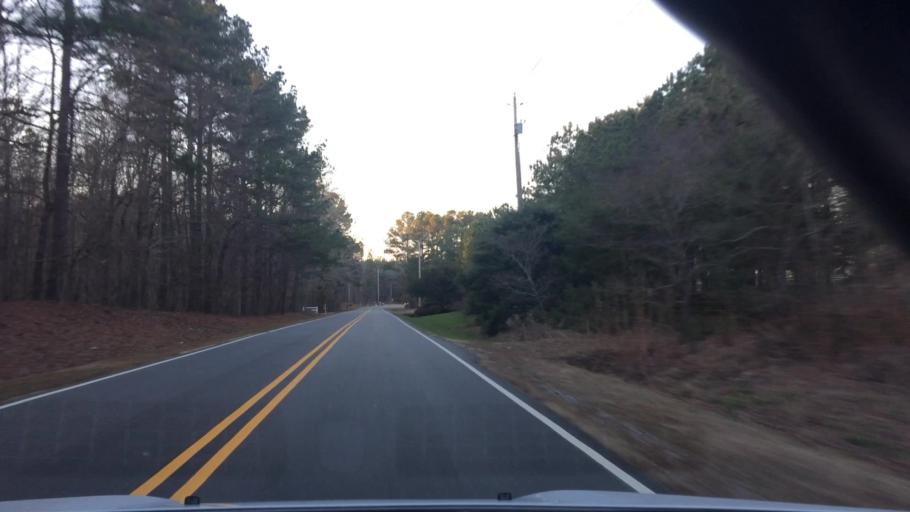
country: US
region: North Carolina
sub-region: Wake County
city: Rolesville
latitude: 35.9487
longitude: -78.4090
